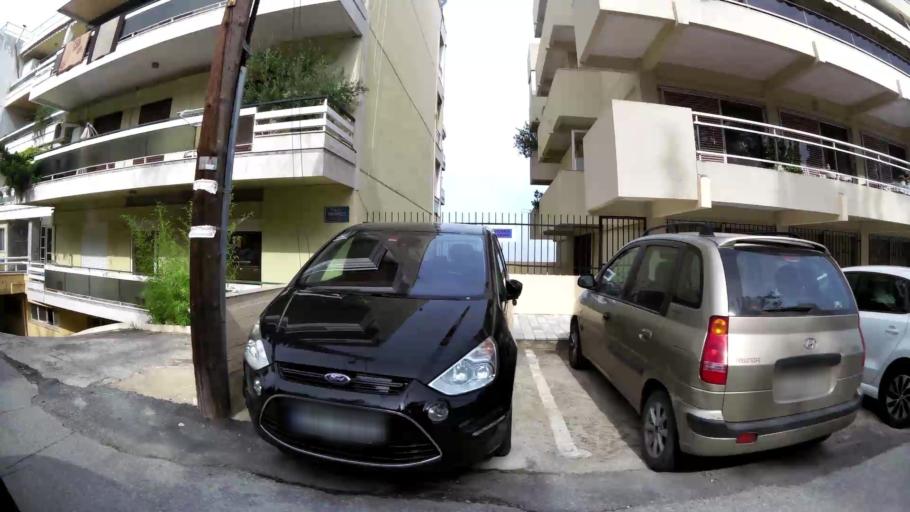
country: GR
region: Central Macedonia
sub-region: Nomos Thessalonikis
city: Panorama
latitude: 40.5886
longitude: 23.0300
